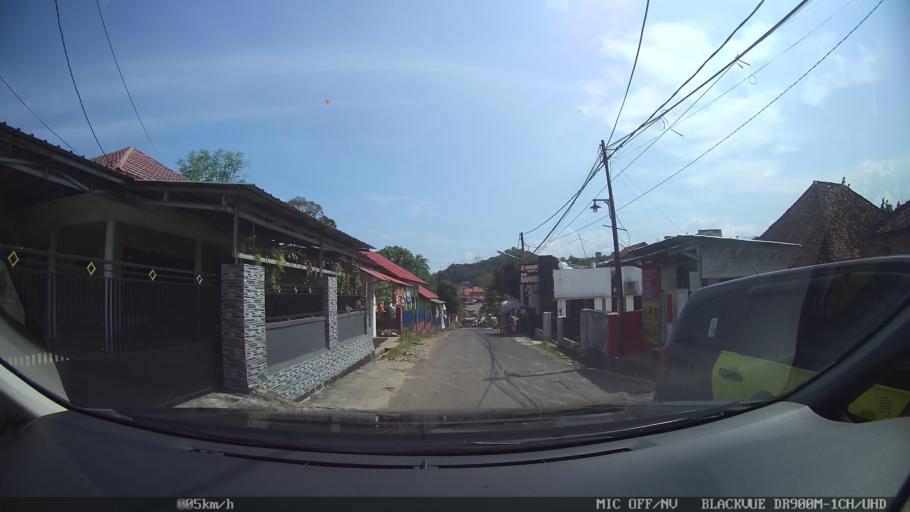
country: ID
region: Lampung
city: Kedaton
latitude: -5.4012
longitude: 105.2500
